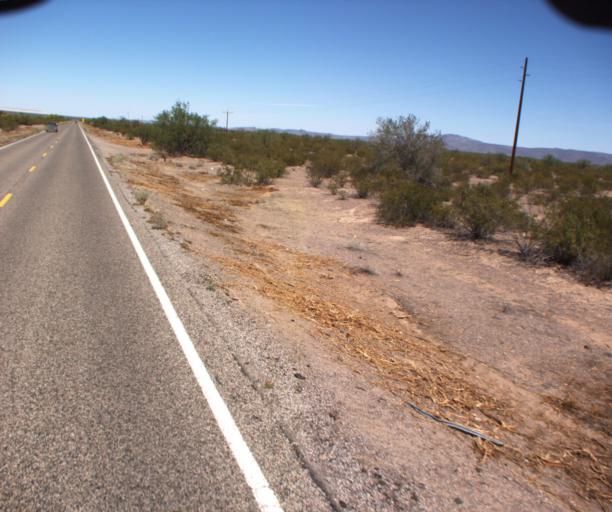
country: US
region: Arizona
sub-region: Pima County
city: Ajo
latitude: 32.2964
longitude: -112.7536
